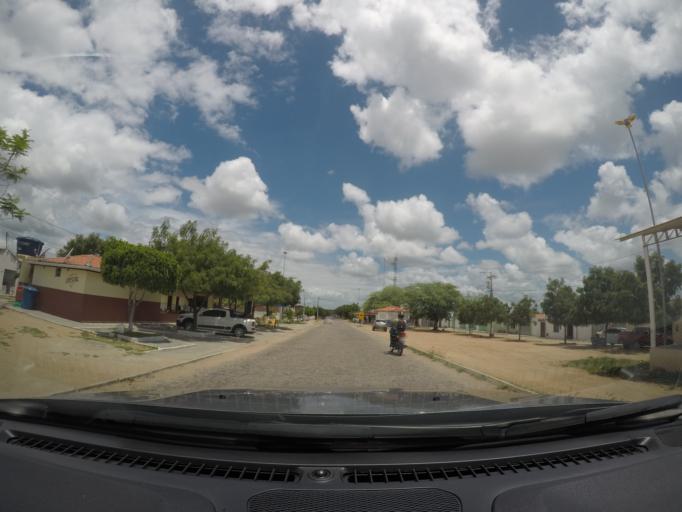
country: BR
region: Bahia
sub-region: Itaberaba
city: Itaberaba
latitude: -12.3624
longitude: -40.0412
